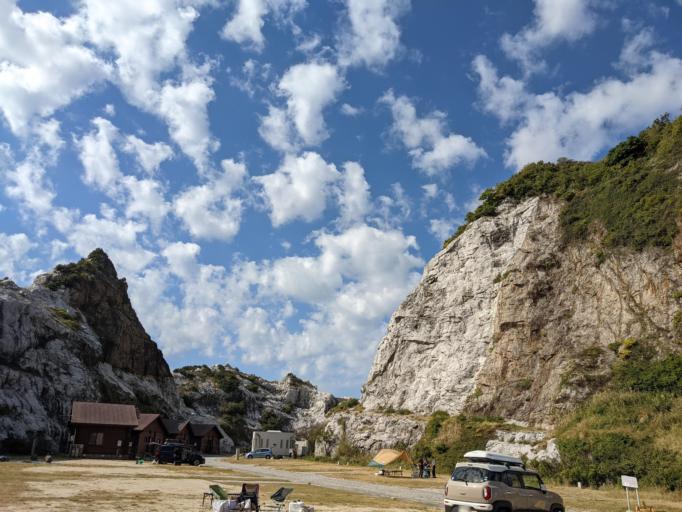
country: JP
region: Wakayama
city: Gobo
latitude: 33.9765
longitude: 135.0722
